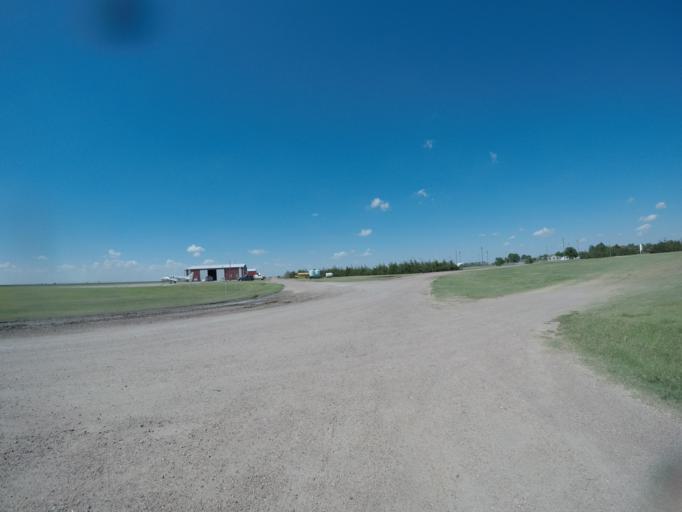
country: US
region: Kansas
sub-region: Sheridan County
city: Hoxie
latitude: 39.3607
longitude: -100.4402
